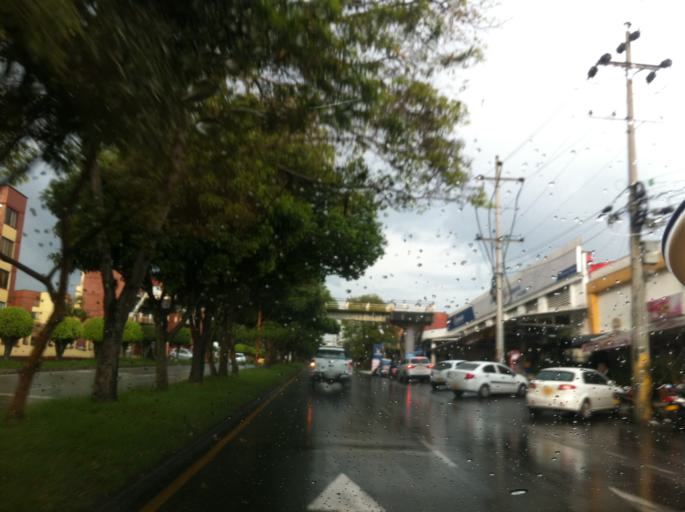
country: CO
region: Quindio
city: Armenia
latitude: 4.5539
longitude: -75.6643
